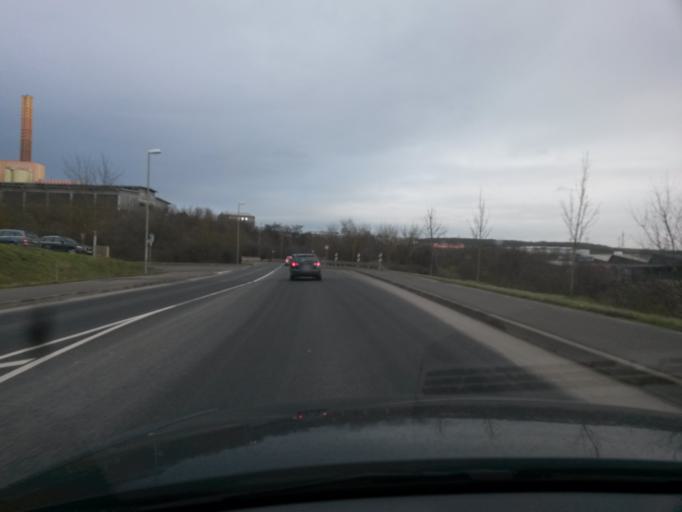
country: DE
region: Bavaria
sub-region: Regierungsbezirk Unterfranken
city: Gerbrunn
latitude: 49.7893
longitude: 9.9937
